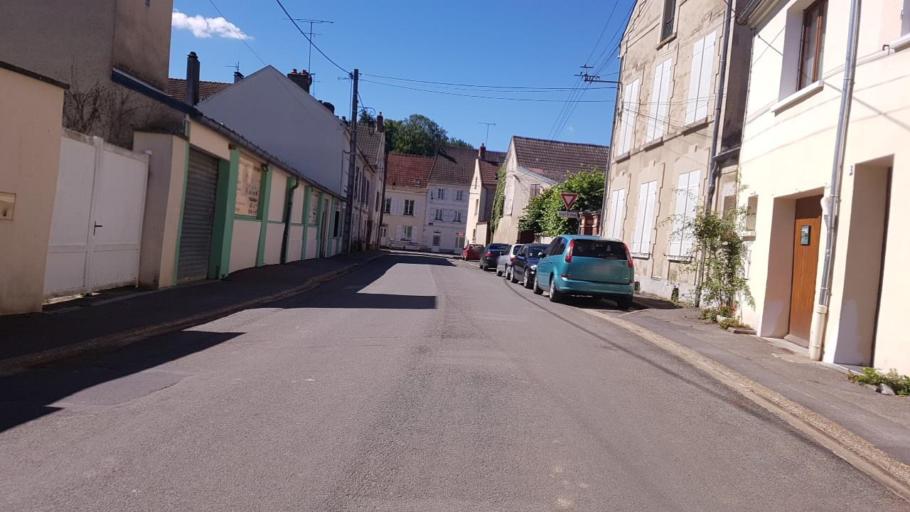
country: FR
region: Picardie
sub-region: Departement de l'Aisne
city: Charly-sur-Marne
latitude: 48.9774
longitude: 3.2826
